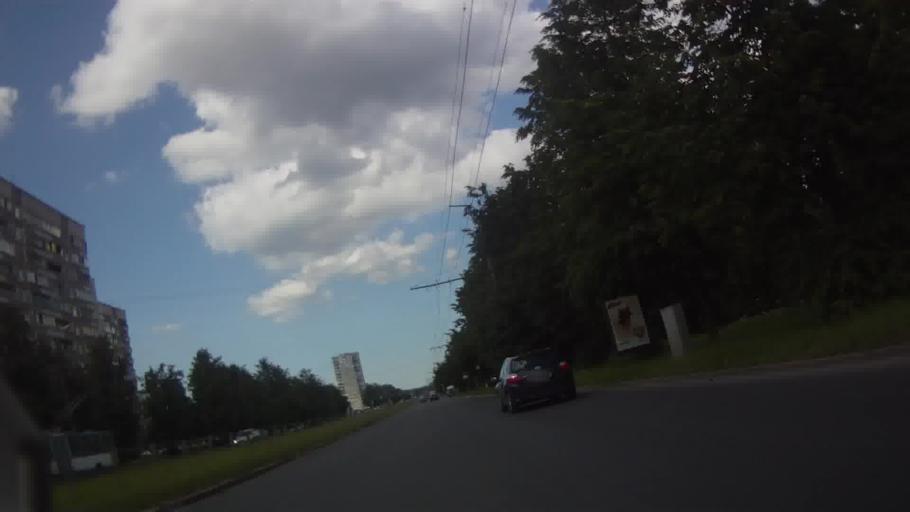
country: LV
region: Stopini
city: Ulbroka
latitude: 56.9357
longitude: 24.2026
